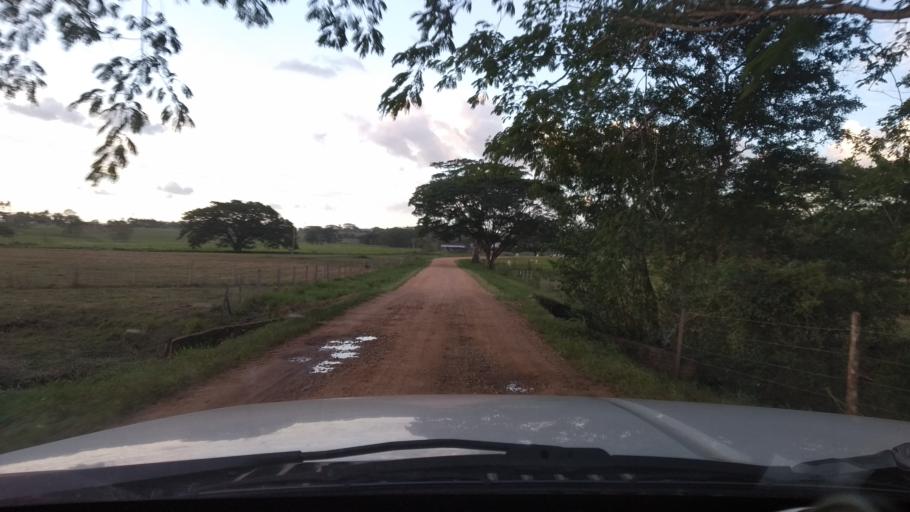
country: BZ
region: Cayo
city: San Ignacio
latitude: 17.2218
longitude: -88.9984
